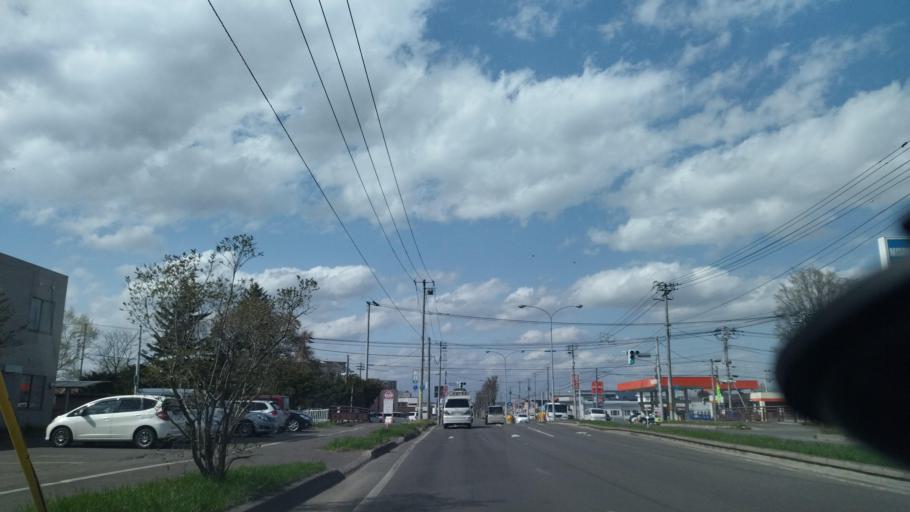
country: JP
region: Hokkaido
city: Obihiro
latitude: 42.9070
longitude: 143.1458
